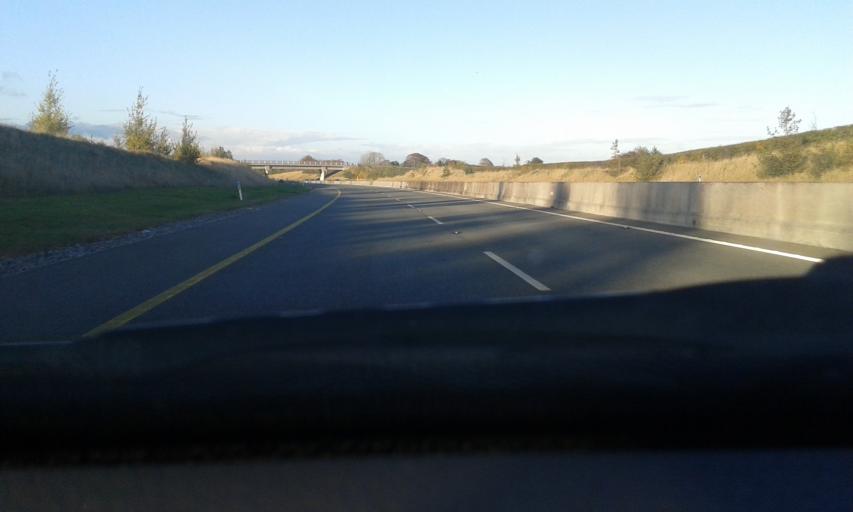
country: IE
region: Leinster
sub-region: Laois
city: Rathdowney
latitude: 52.8109
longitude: -7.4944
